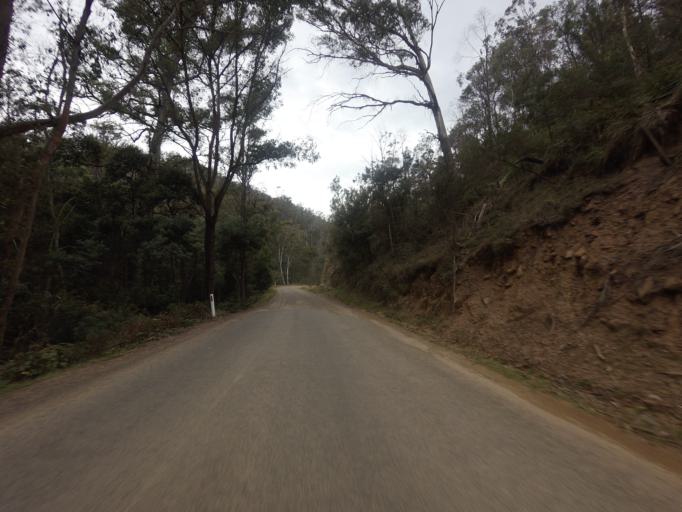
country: AU
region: Tasmania
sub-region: Derwent Valley
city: New Norfolk
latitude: -42.5863
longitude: 147.0176
